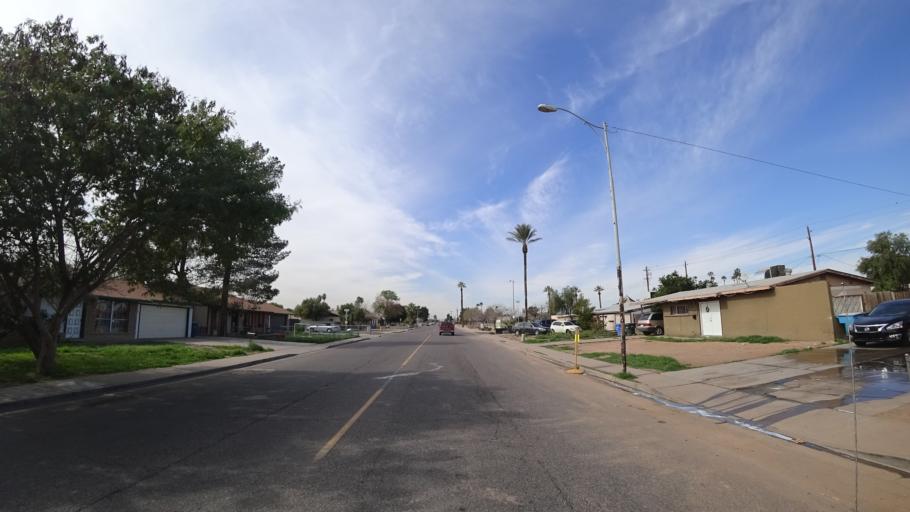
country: US
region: Arizona
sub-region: Maricopa County
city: Tolleson
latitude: 33.4873
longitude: -112.2263
